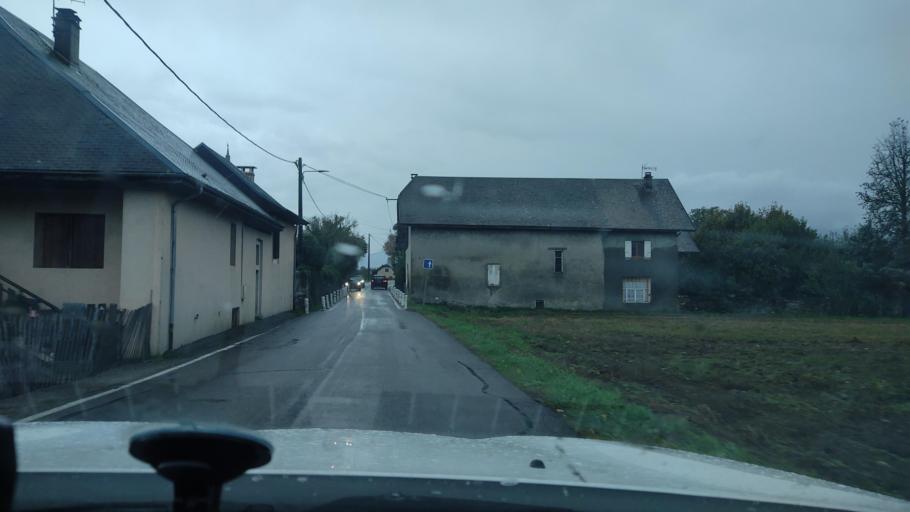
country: FR
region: Rhone-Alpes
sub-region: Departement de la Savoie
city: Cruet
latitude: 45.4989
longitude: 6.0861
